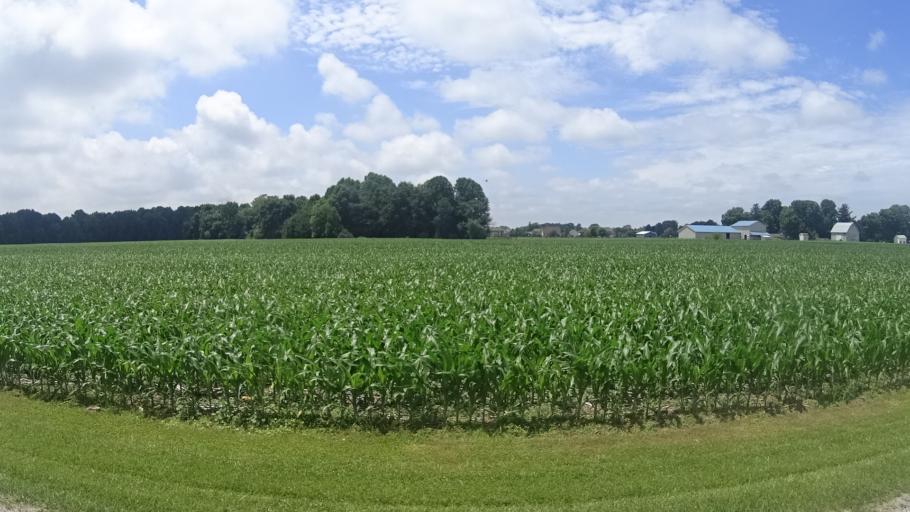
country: US
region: Ohio
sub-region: Erie County
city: Milan
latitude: 41.2953
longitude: -82.5719
